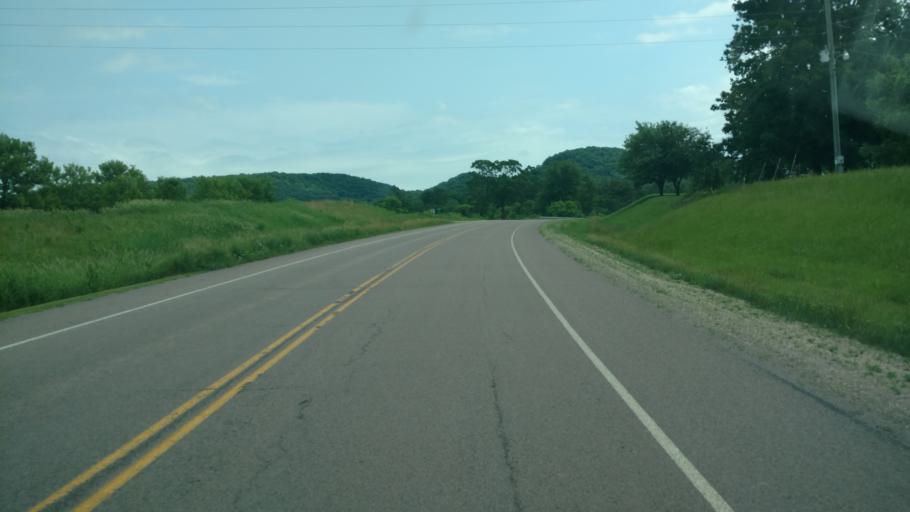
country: US
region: Wisconsin
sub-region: Monroe County
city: Cashton
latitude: 43.6921
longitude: -90.5973
